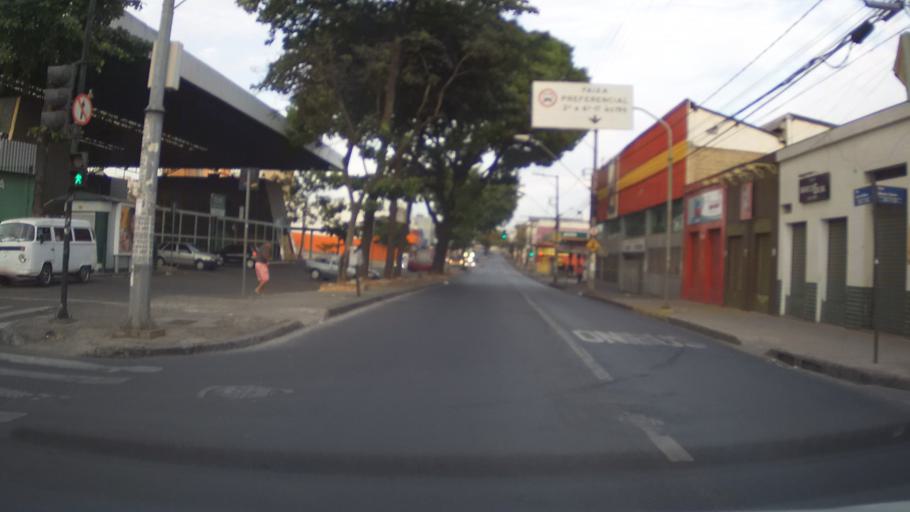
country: BR
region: Minas Gerais
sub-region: Belo Horizonte
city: Belo Horizonte
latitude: -19.9143
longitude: -43.9880
